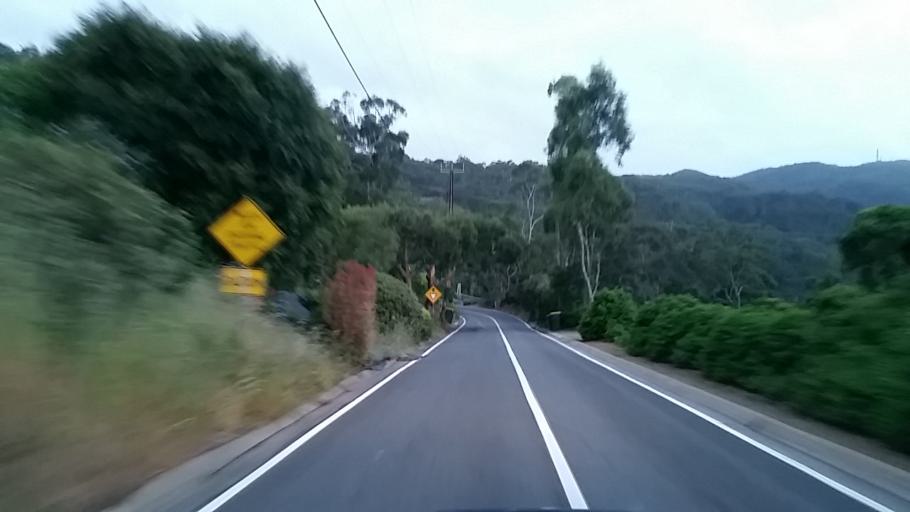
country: AU
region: South Australia
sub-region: Burnside
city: Beaumont
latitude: -34.9511
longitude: 138.6866
